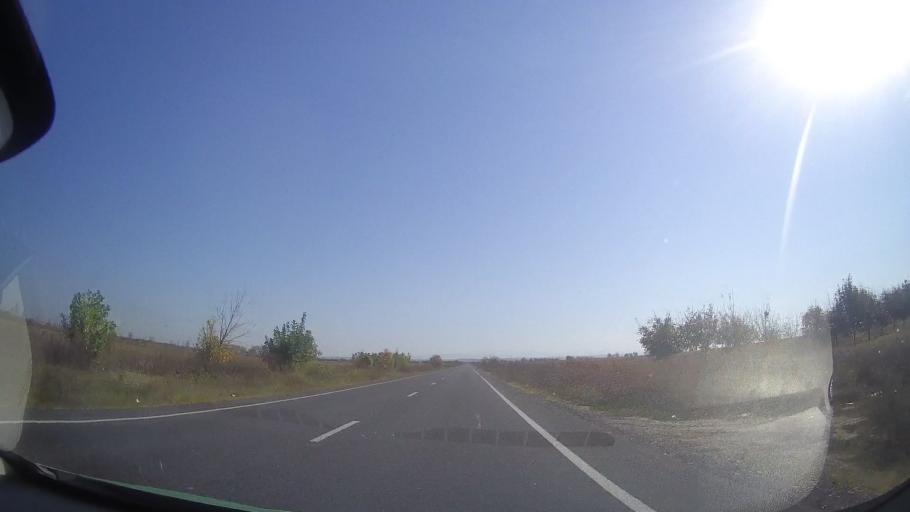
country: RO
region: Timis
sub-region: Comuna Costeiu
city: Costeiu
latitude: 45.7440
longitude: 21.8120
